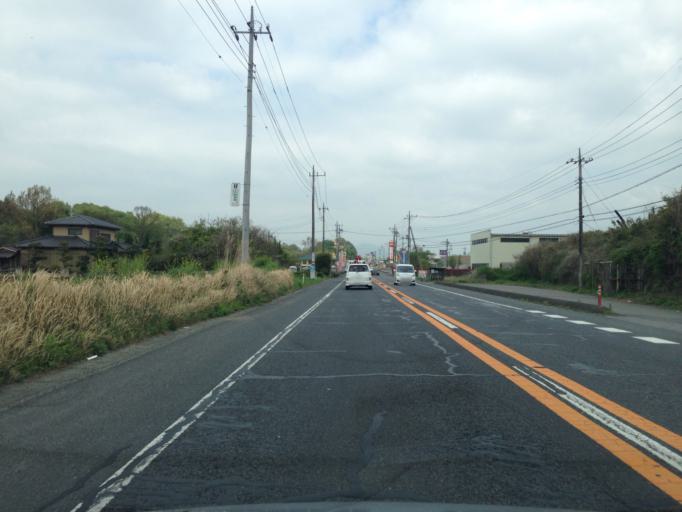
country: JP
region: Ibaraki
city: Iwase
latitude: 36.3459
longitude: 140.0457
